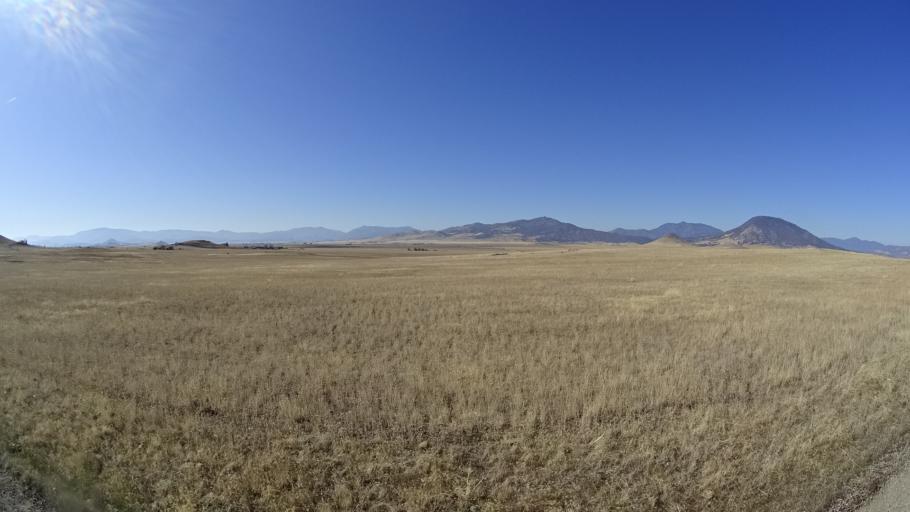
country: US
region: California
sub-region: Siskiyou County
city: Montague
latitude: 41.7998
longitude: -122.4158
